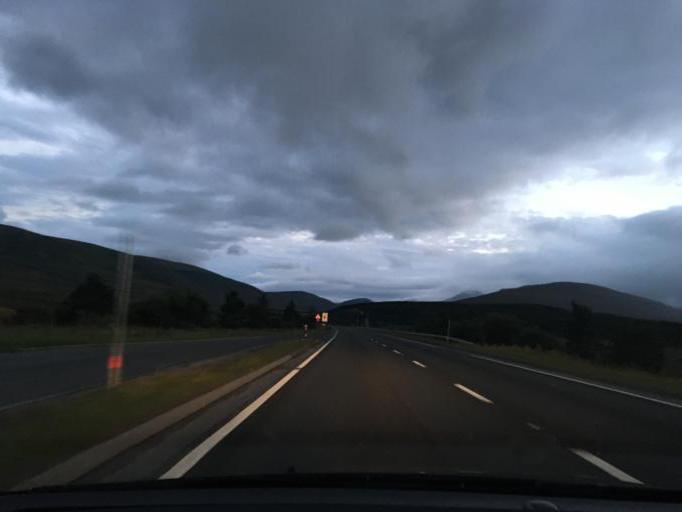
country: GB
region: Scotland
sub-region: Highland
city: Kingussie
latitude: 56.9311
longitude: -4.2349
